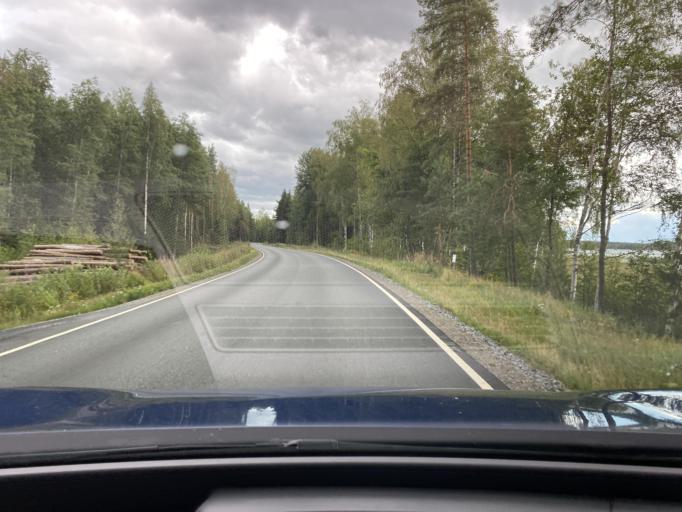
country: FI
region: Pirkanmaa
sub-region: Lounais-Pirkanmaa
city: Vammala
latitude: 61.3014
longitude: 22.9585
